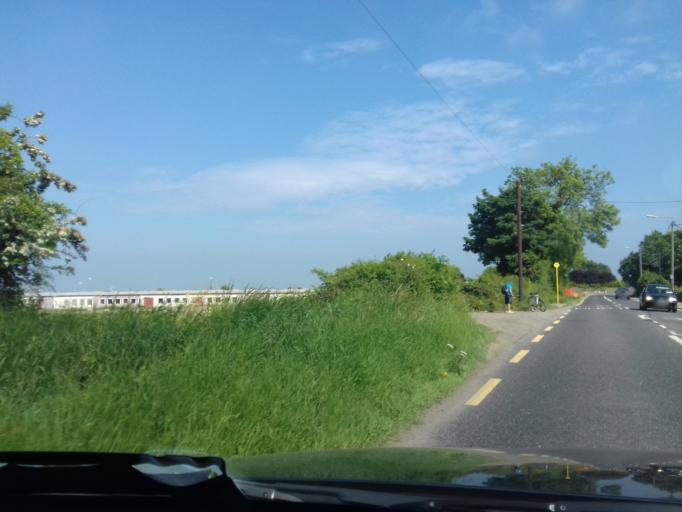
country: IE
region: Leinster
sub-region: Fingal County
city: Swords
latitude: 53.4722
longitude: -6.2521
